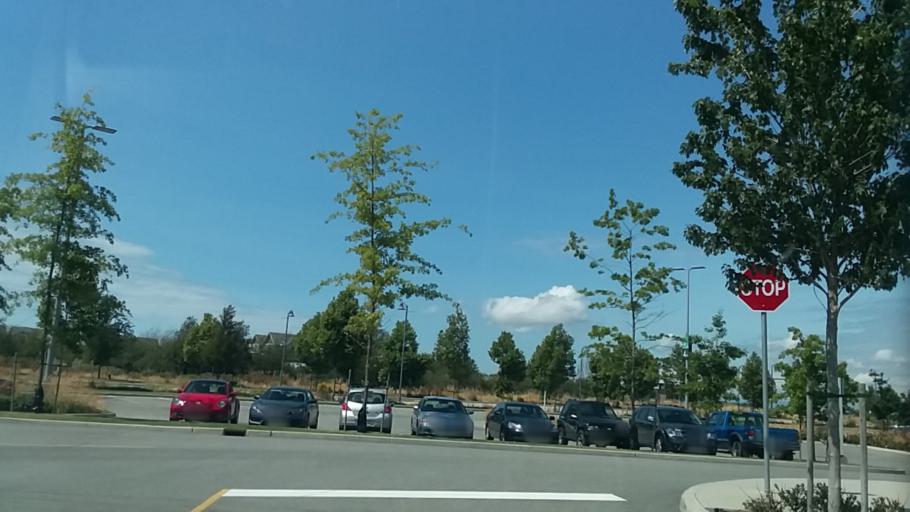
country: US
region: Washington
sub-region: Whatcom County
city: Point Roberts
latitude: 49.0364
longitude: -123.0895
